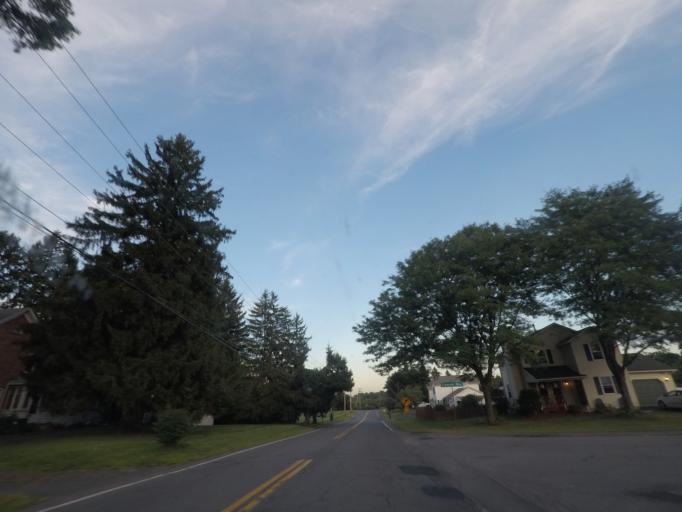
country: US
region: New York
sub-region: Albany County
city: Cohoes
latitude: 42.7649
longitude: -73.7717
